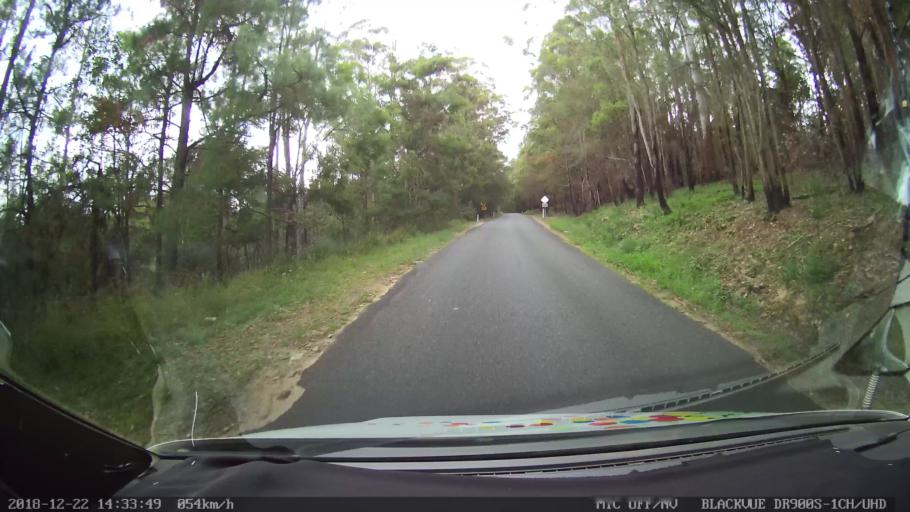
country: AU
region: New South Wales
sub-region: Bellingen
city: Dorrigo
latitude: -30.1155
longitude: 152.6220
